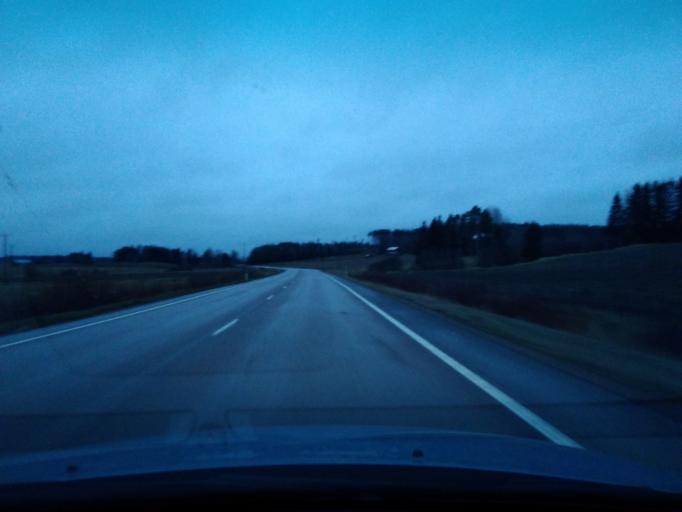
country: FI
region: Uusimaa
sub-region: Porvoo
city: Askola
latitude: 60.4618
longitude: 25.5782
